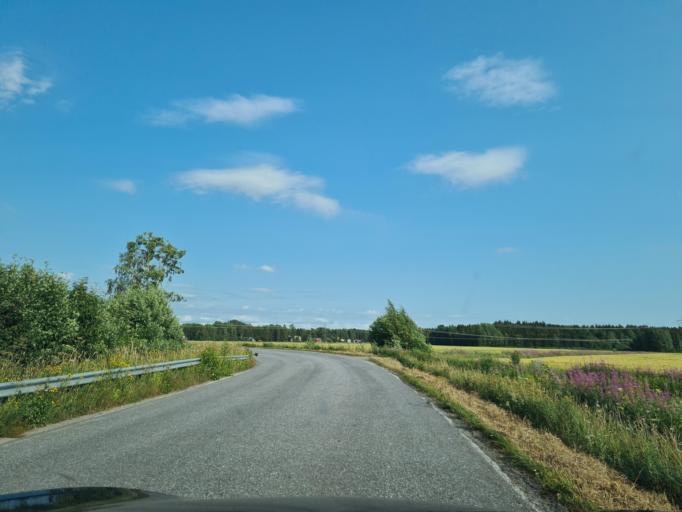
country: FI
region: Ostrobothnia
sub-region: Vaasa
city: Ristinummi
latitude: 63.0295
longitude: 21.8317
